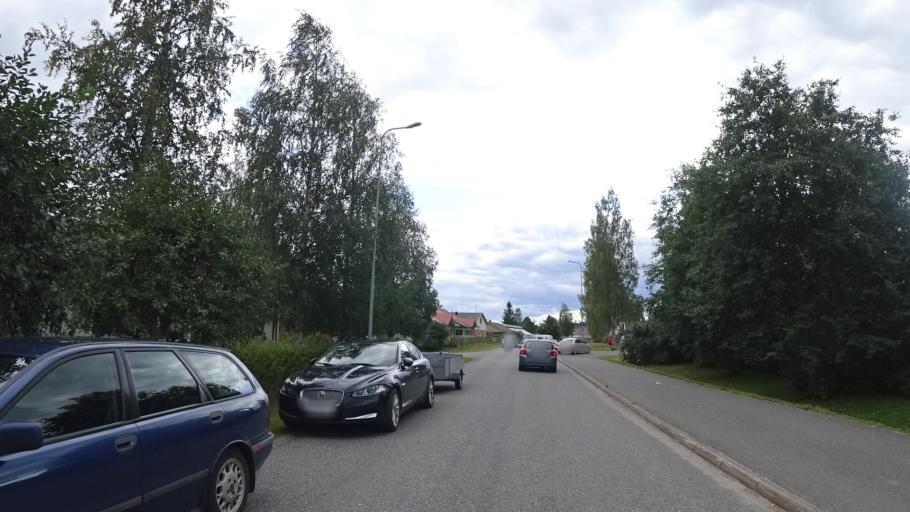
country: FI
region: North Karelia
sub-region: Joensuu
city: Ilomantsi
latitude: 62.6716
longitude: 30.9367
